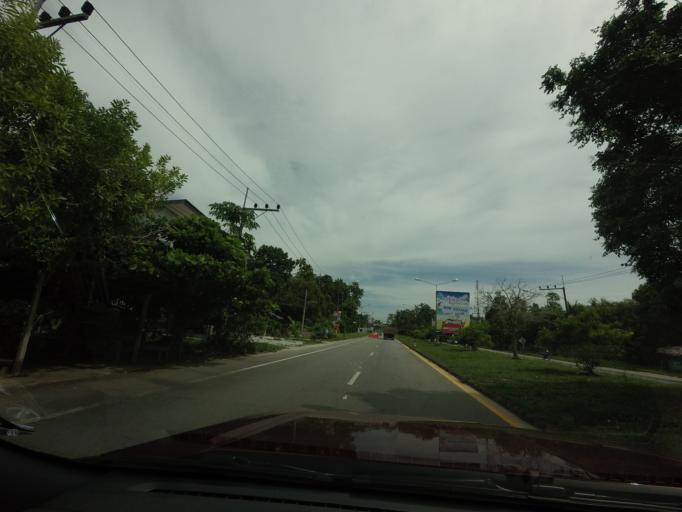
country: TH
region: Narathiwat
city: Tak Bai
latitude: 6.2589
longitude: 102.0452
